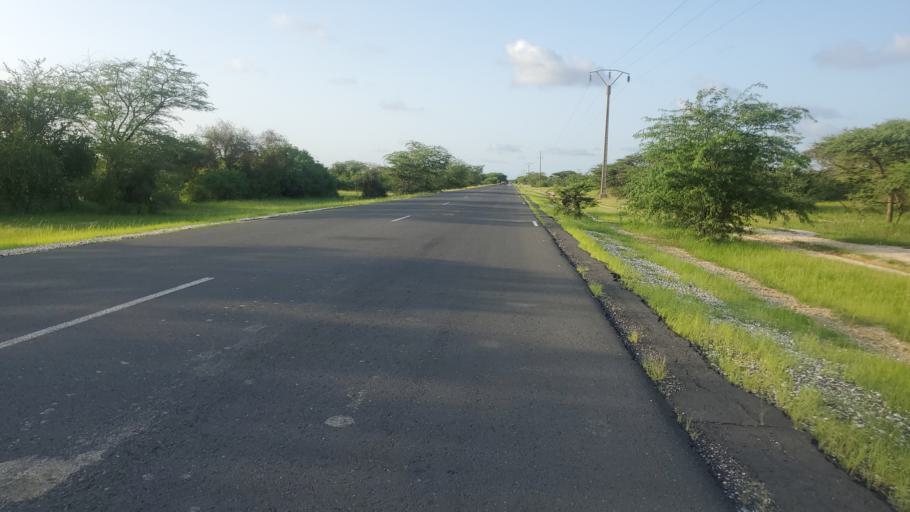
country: SN
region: Saint-Louis
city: Saint-Louis
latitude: 16.1820
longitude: -16.4094
